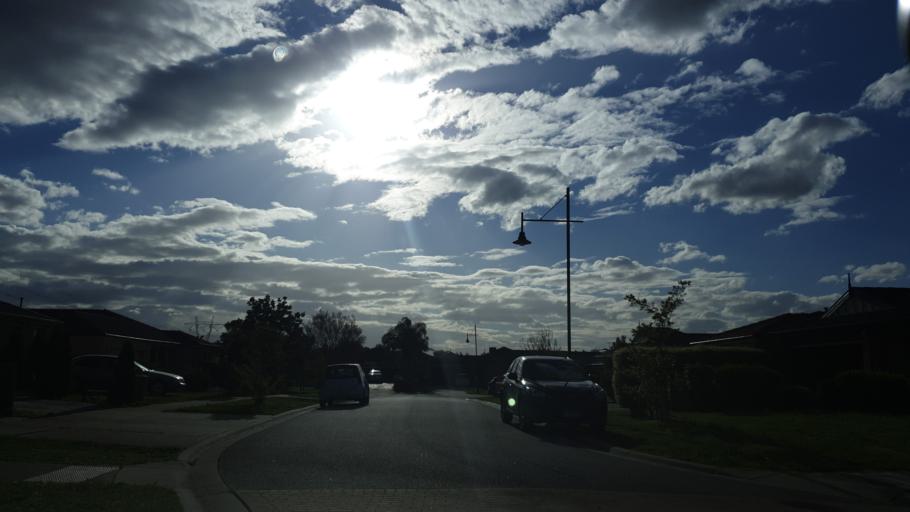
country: AU
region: Victoria
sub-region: Casey
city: Cranbourne North
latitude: -38.0888
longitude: 145.2875
